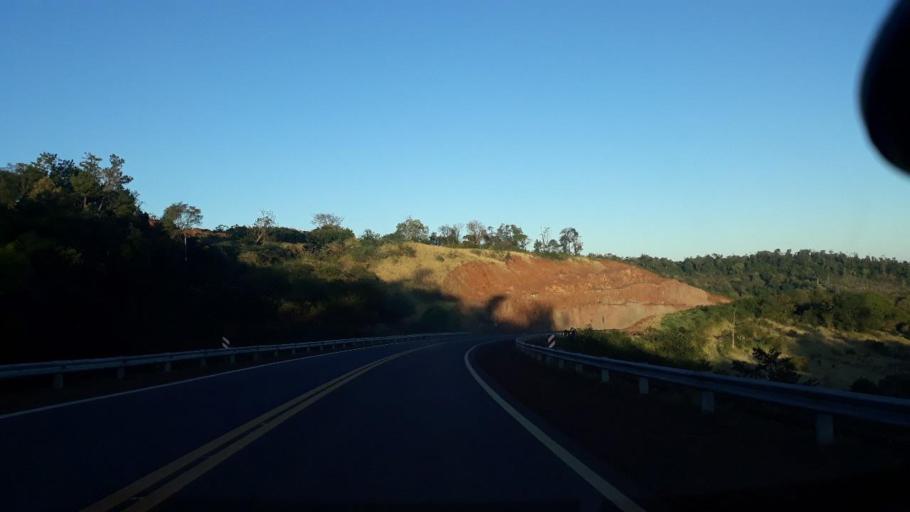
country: AR
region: Misiones
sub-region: Departamento de San Pedro
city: San Pedro
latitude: -26.5390
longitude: -53.9424
